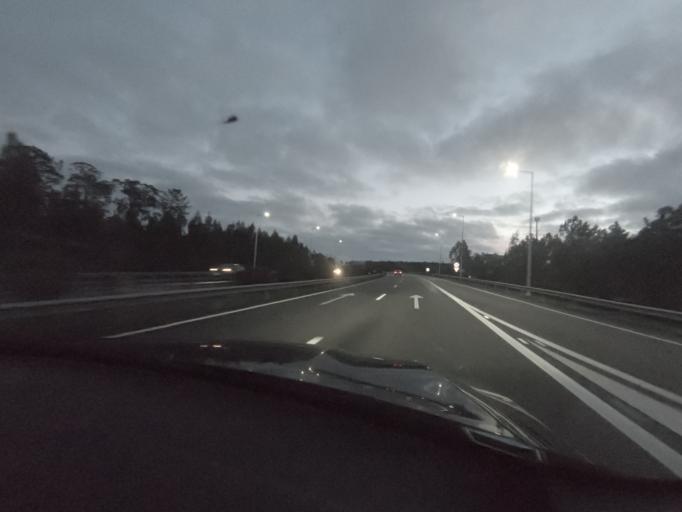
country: PT
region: Leiria
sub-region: Pombal
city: Pombal
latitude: 39.9383
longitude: -8.6798
